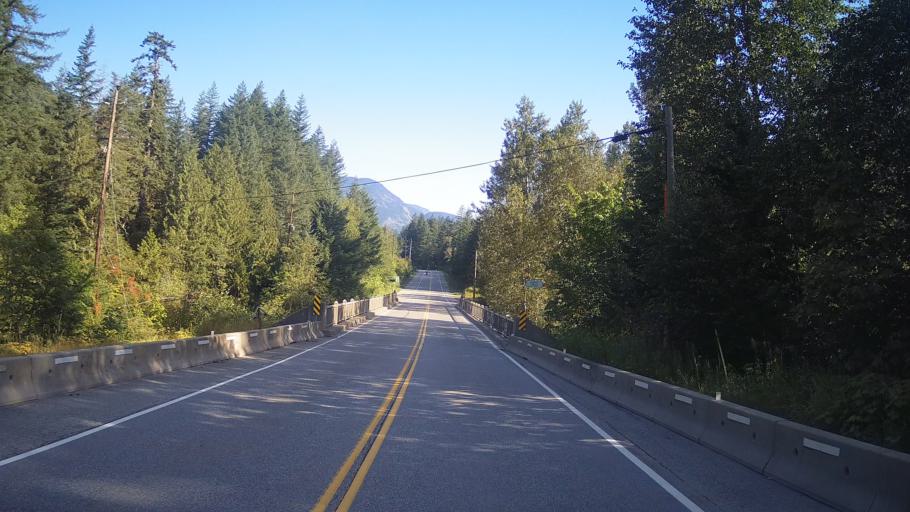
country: CA
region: British Columbia
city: Hope
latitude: 49.5085
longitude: -121.4173
